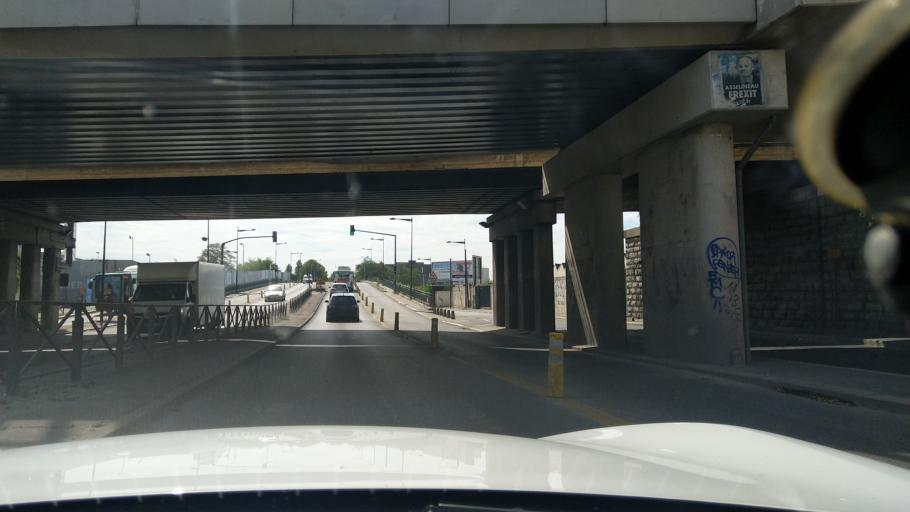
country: FR
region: Ile-de-France
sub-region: Departement de Seine-Saint-Denis
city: Le Bourget
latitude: 48.9317
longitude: 2.4223
